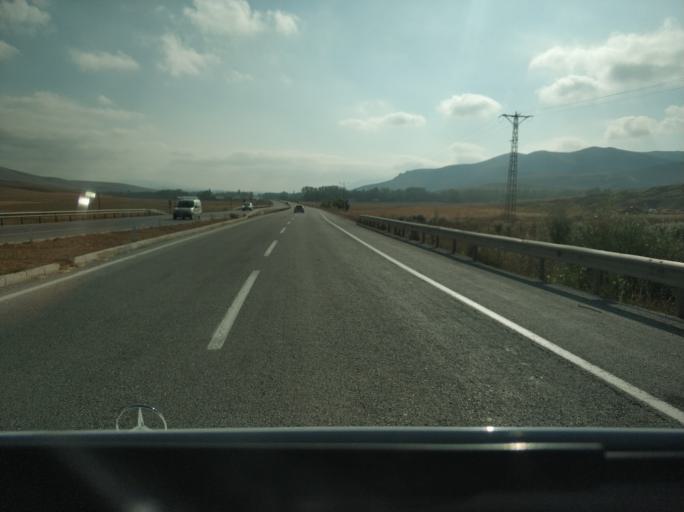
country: TR
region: Sivas
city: Yildizeli
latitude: 39.8363
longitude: 36.4469
